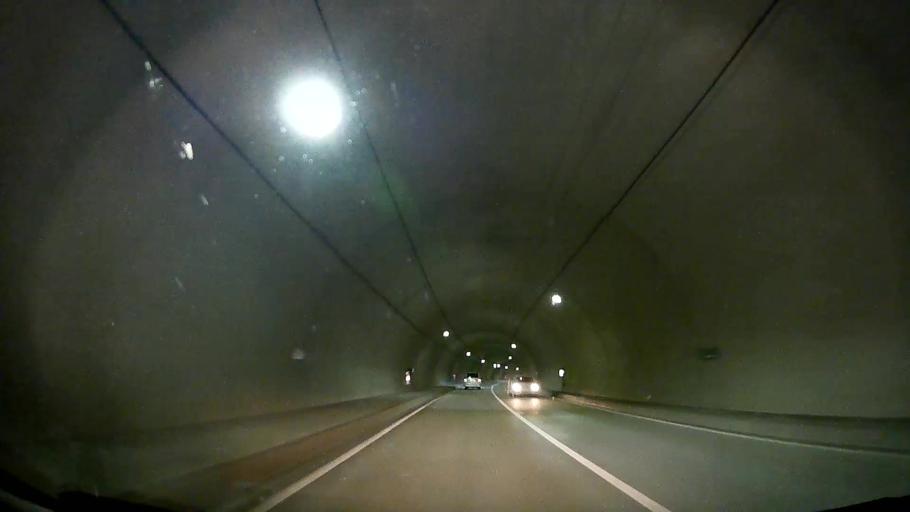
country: JP
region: Hokkaido
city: Otaru
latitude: 43.2072
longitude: 140.8892
